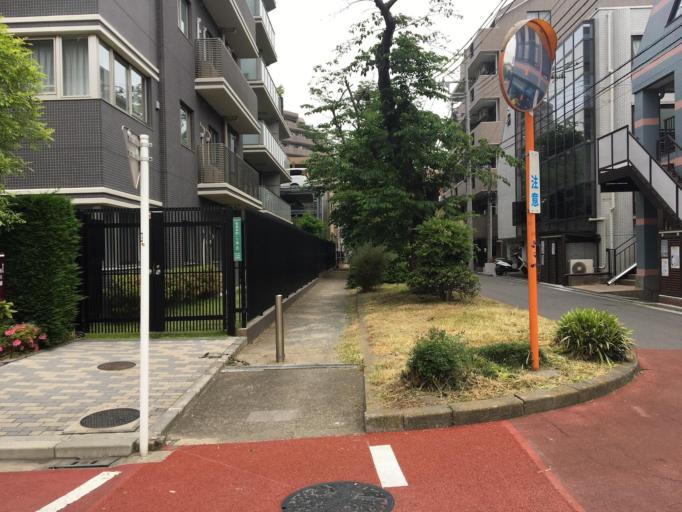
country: JP
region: Tokyo
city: Chofugaoka
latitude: 35.6359
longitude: 139.5796
